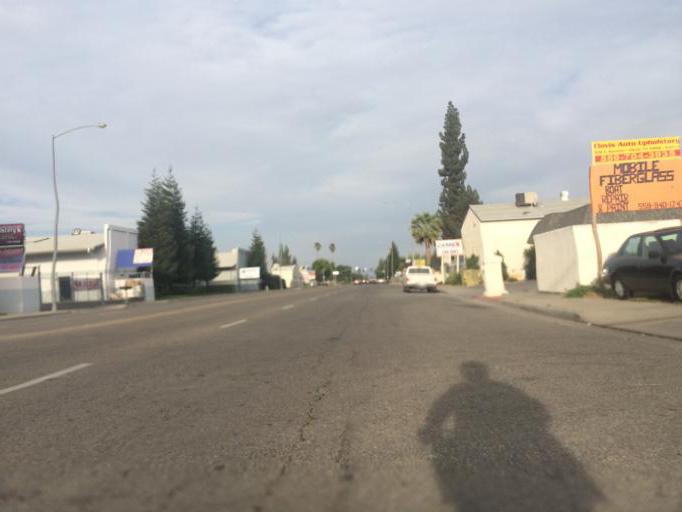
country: US
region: California
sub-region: Fresno County
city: Clovis
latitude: 36.8158
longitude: -119.6942
